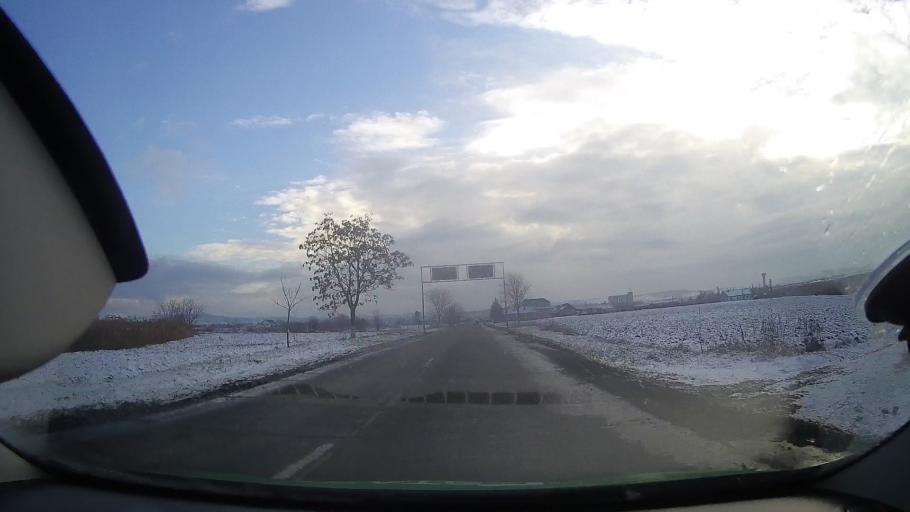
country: RO
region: Mures
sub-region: Comuna Iernut
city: Iernut
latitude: 46.4429
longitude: 24.2517
